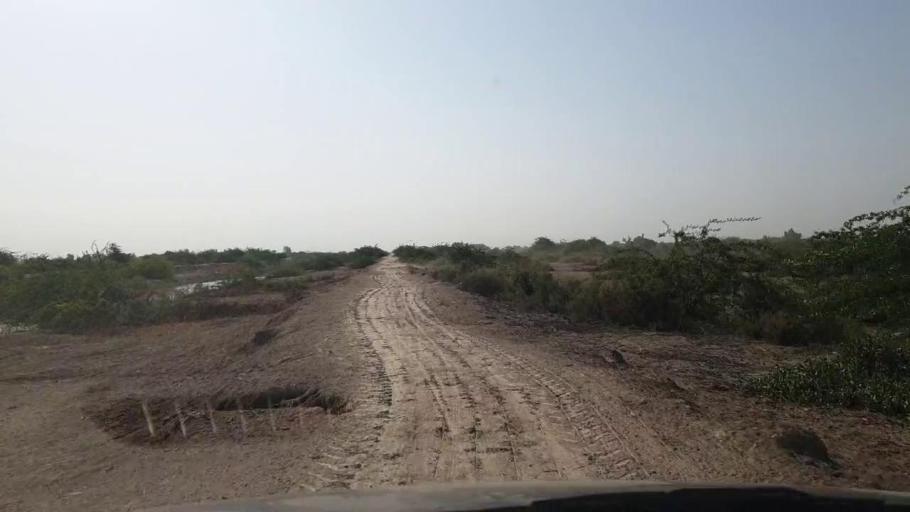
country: PK
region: Sindh
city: Kadhan
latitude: 24.5809
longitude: 69.0796
